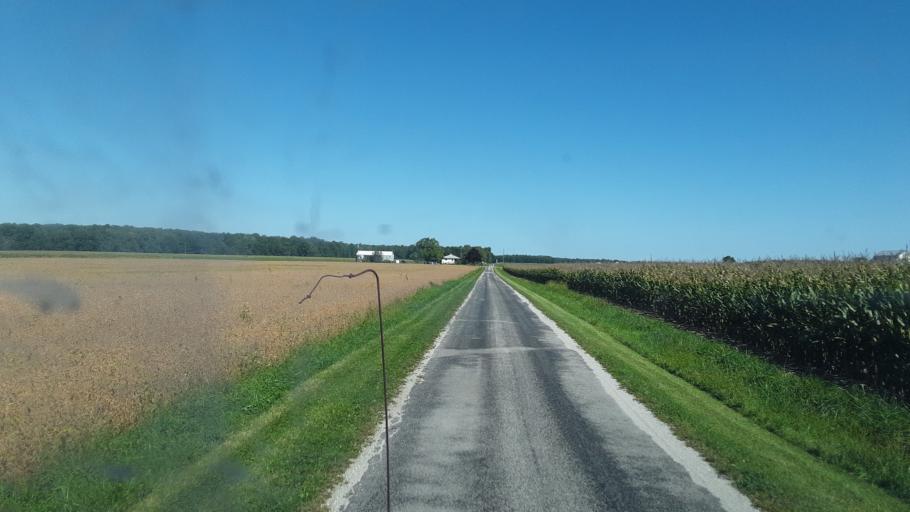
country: US
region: Ohio
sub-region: Crawford County
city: Bucyrus
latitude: 40.9762
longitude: -83.0355
